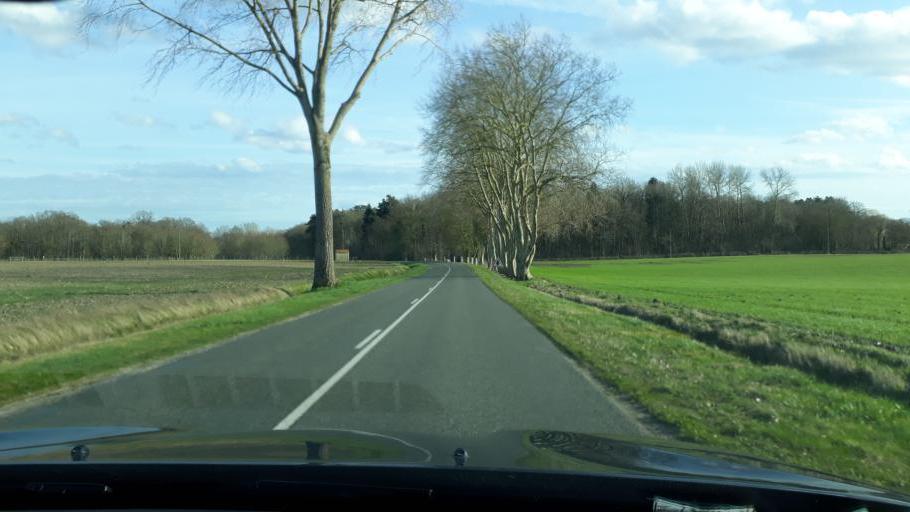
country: FR
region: Centre
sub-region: Departement du Loiret
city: Chilleurs-aux-Bois
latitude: 48.0638
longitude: 2.1521
